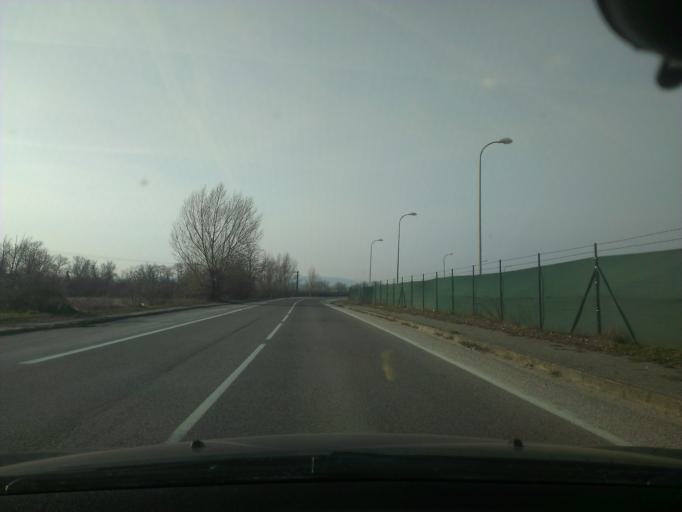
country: SK
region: Trnavsky
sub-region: Okres Trnava
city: Piestany
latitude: 48.6667
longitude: 17.8752
